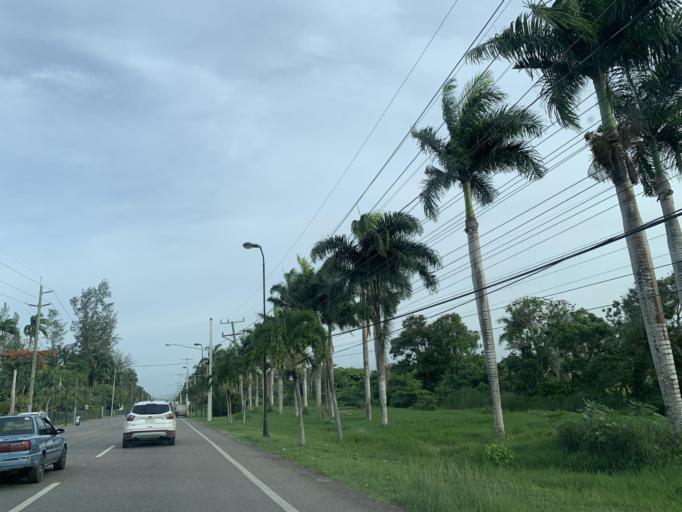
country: DO
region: Puerto Plata
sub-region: Puerto Plata
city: Puerto Plata
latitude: 19.7659
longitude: -70.6504
